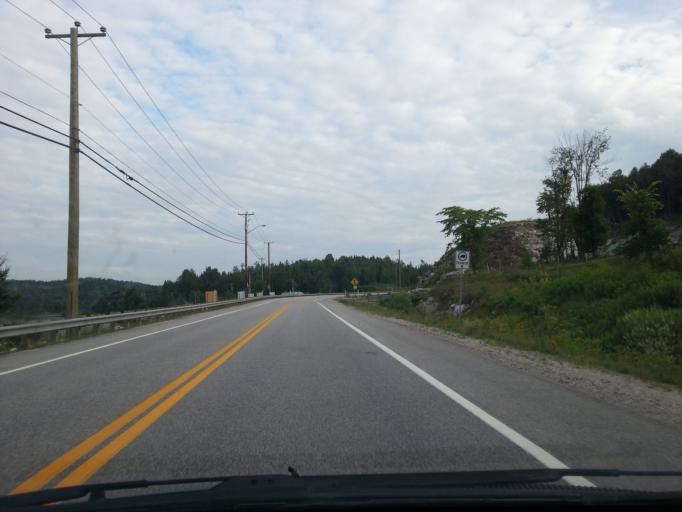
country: CA
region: Quebec
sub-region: Outaouais
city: Wakefield
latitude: 45.7334
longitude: -75.9074
